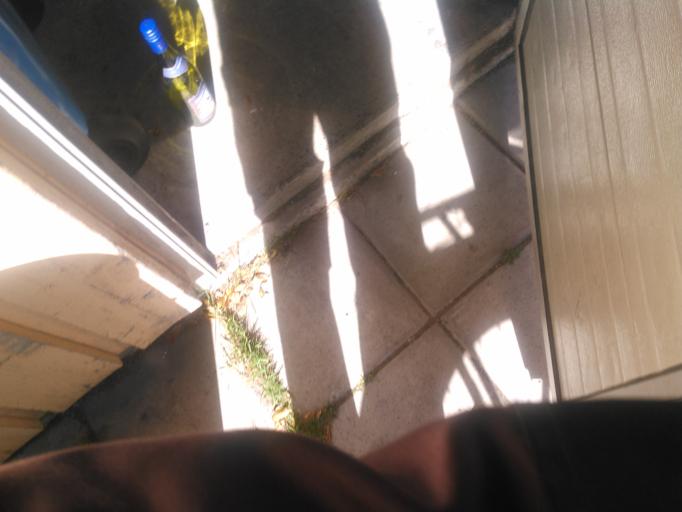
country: SE
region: Vaesterbotten
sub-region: Umea Kommun
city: Umea
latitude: 63.8134
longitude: 20.3184
